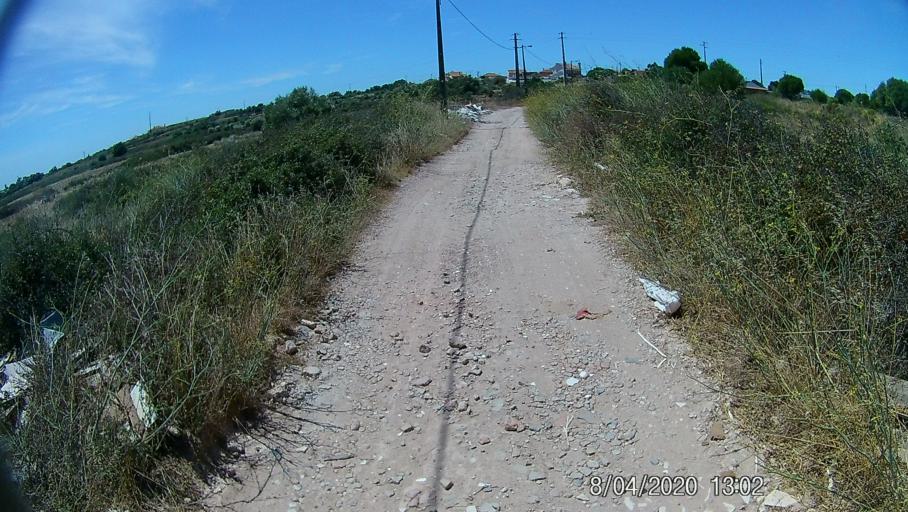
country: PT
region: Lisbon
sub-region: Sintra
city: Rio de Mouro
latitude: 38.7415
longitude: -9.3545
